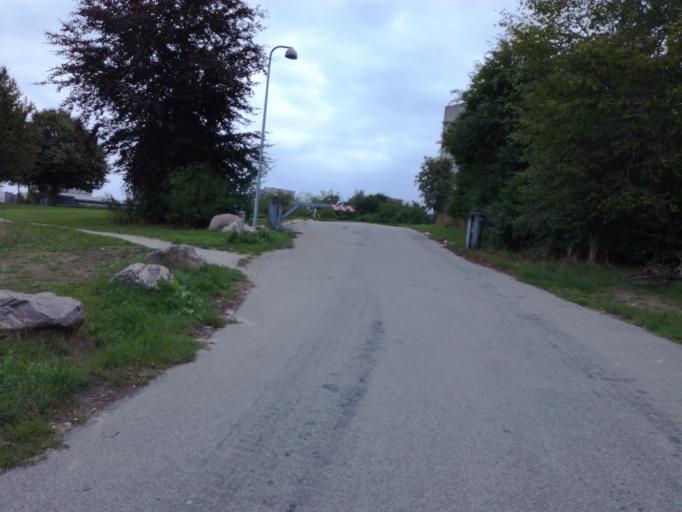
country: DK
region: South Denmark
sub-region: Fredericia Kommune
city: Fredericia
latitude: 55.5735
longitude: 9.7281
